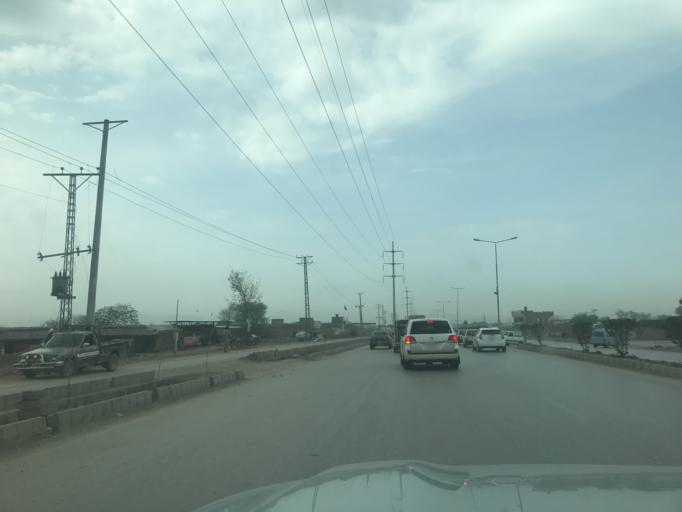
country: PK
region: Khyber Pakhtunkhwa
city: Peshawar
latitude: 33.9735
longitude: 71.5457
